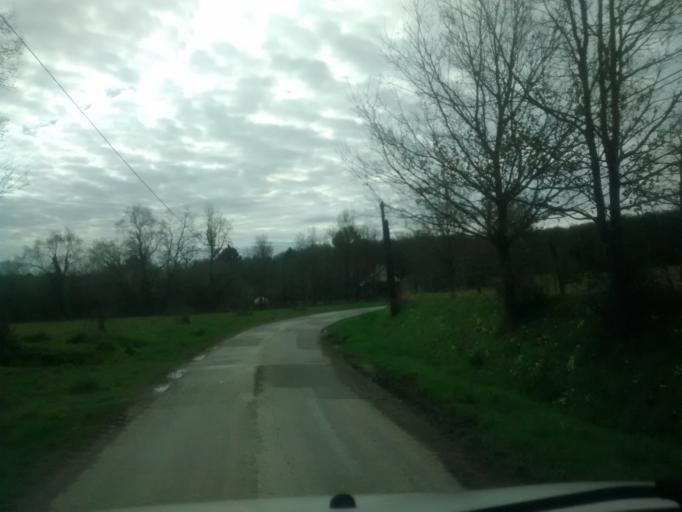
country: FR
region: Brittany
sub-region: Departement d'Ille-et-Vilaine
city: Chasne-sur-Illet
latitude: 48.2335
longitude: -1.5442
